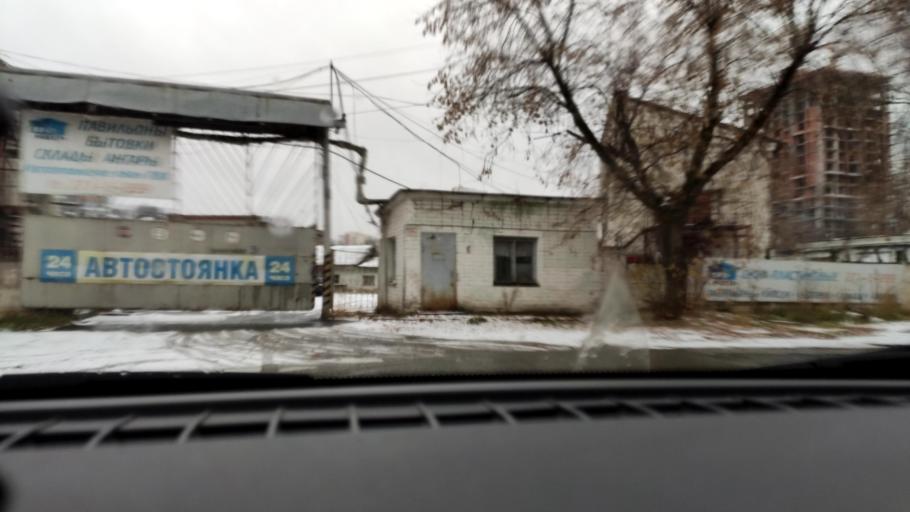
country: RU
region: Perm
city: Perm
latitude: 58.0009
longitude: 56.1845
